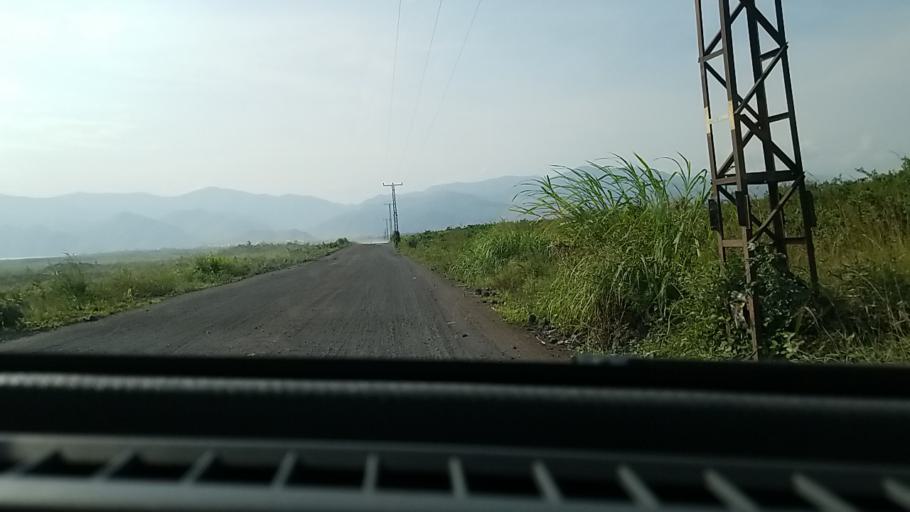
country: CD
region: Nord Kivu
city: Sake
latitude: -1.5895
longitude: 29.0949
